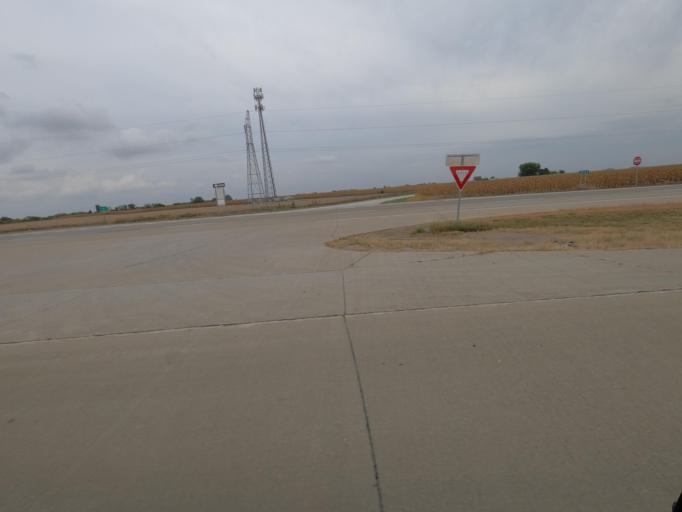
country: US
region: Iowa
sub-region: Jasper County
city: Monroe
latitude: 41.5078
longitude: -93.0846
